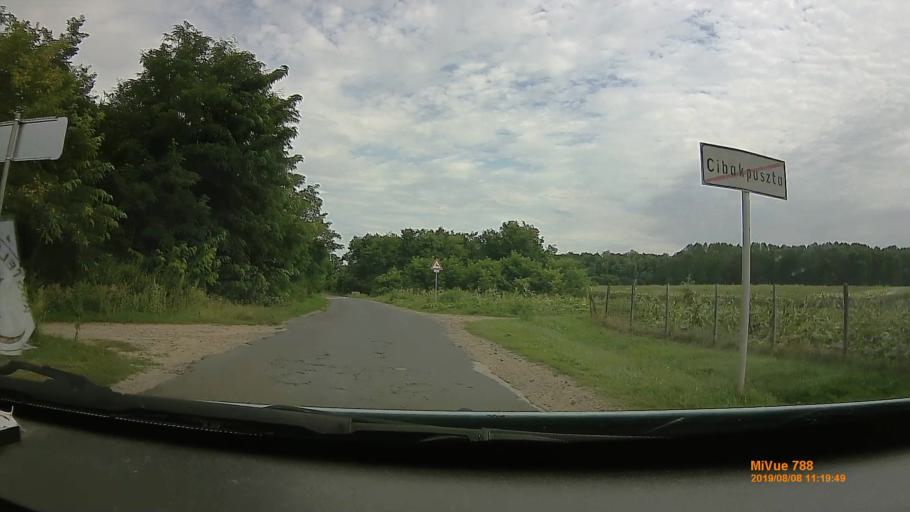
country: HU
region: Szabolcs-Szatmar-Bereg
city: Balkany
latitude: 47.7479
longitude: 21.8413
